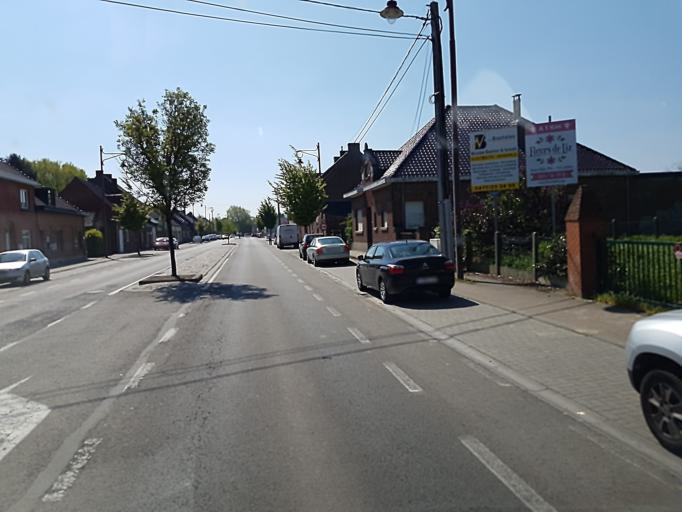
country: BE
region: Wallonia
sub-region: Province du Hainaut
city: Jurbise
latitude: 50.5273
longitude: 3.9135
